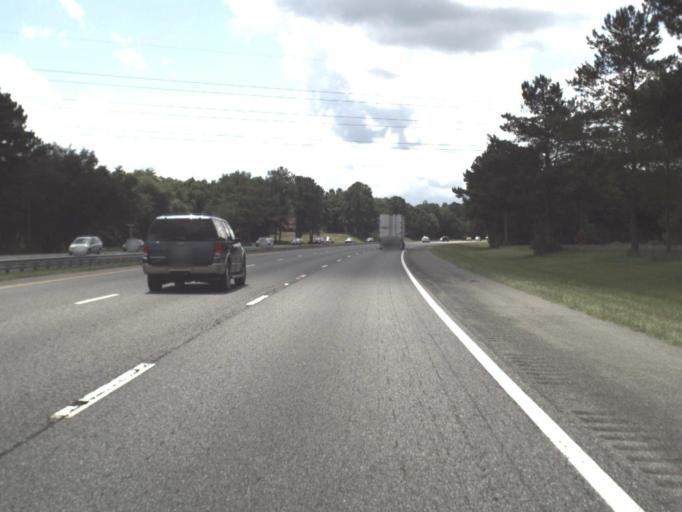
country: US
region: Florida
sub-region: Columbia County
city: Five Points
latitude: 30.2201
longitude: -82.7111
